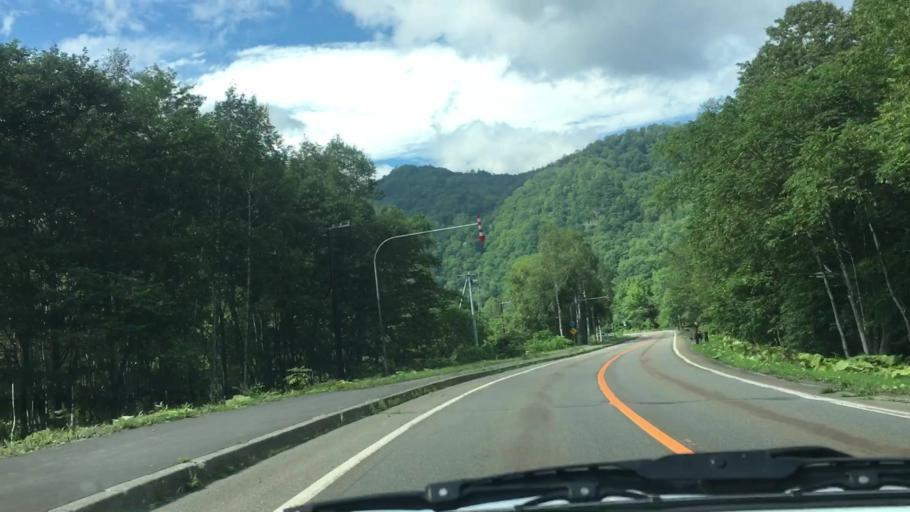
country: JP
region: Hokkaido
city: Otofuke
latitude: 43.3569
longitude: 143.2551
